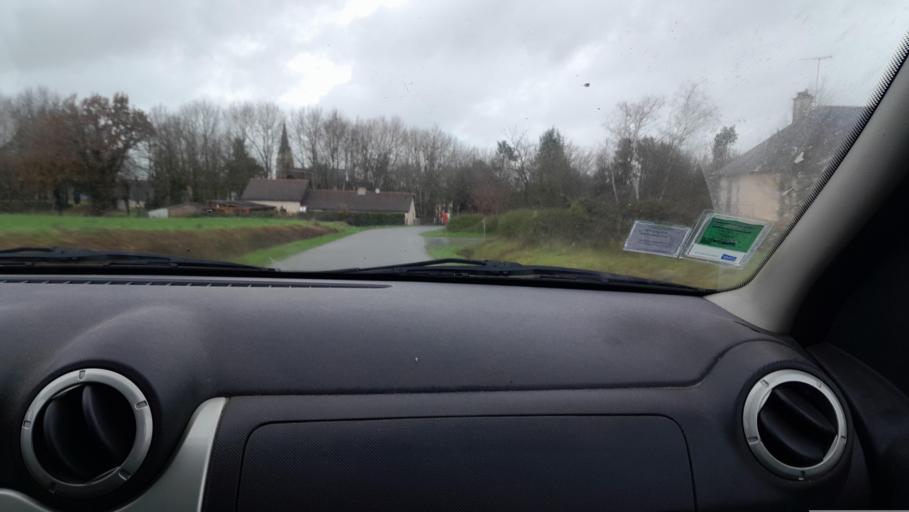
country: FR
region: Pays de la Loire
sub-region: Departement de la Mayenne
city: Ballots
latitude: 47.9057
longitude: -1.1398
